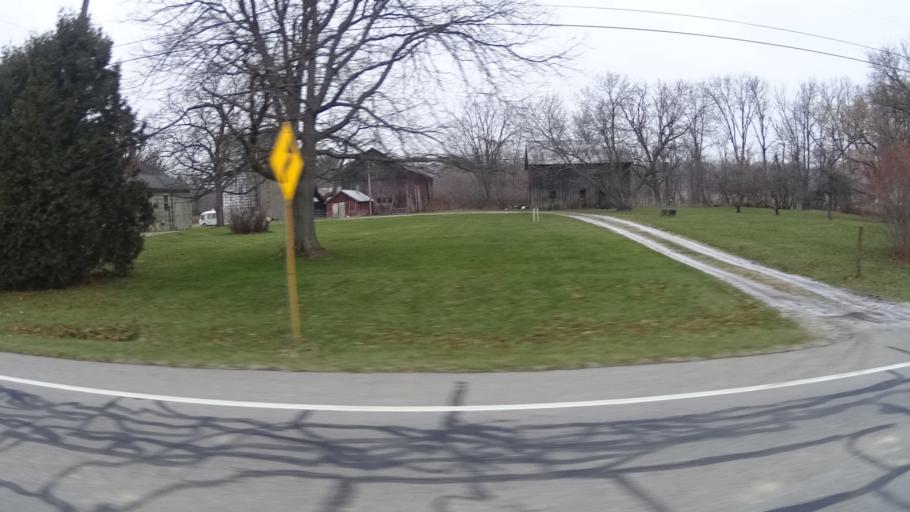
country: US
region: Ohio
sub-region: Lorain County
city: Oberlin
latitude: 41.3021
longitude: -82.2732
